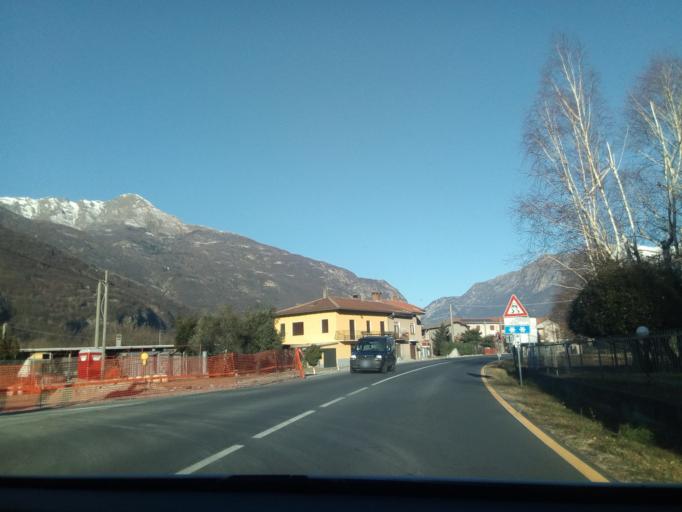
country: IT
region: Piedmont
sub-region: Provincia di Torino
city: Settimo Vittone
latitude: 45.5374
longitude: 7.8375
